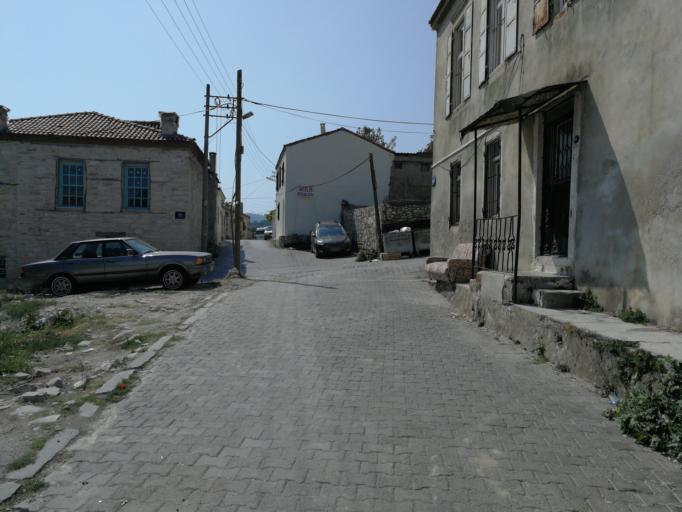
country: TR
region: Izmir
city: Urla
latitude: 38.3208
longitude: 26.7655
